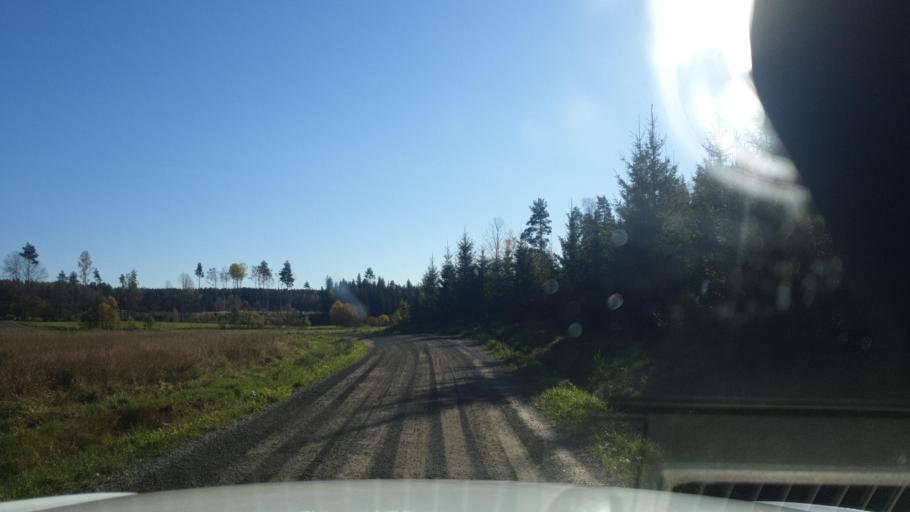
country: SE
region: Vaermland
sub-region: Grums Kommun
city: Grums
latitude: 59.5386
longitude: 12.8755
